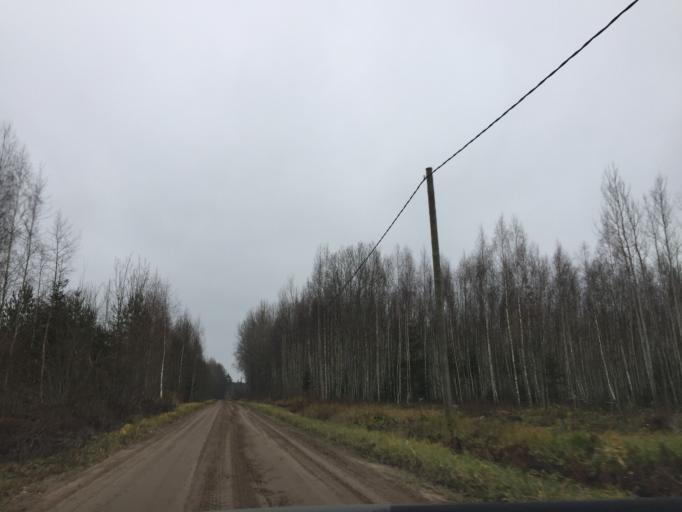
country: LV
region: Limbazu Rajons
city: Limbazi
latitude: 57.5033
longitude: 24.7642
